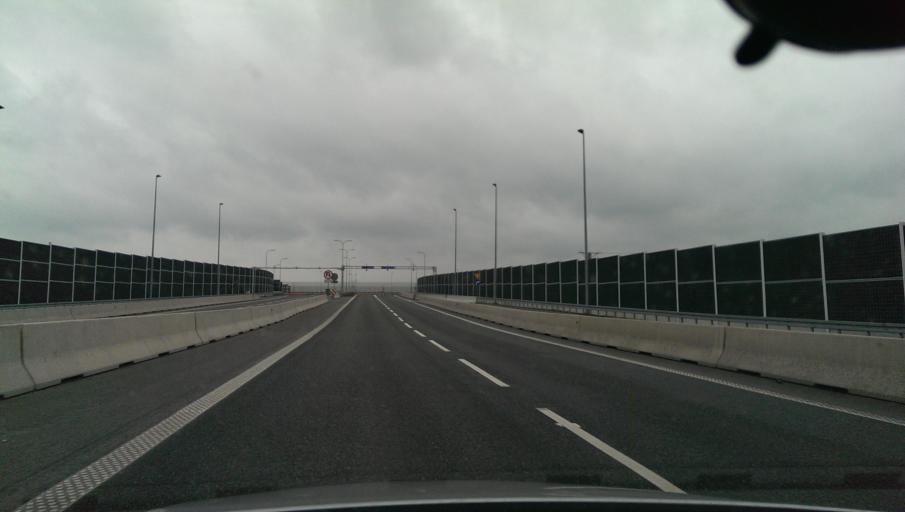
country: PL
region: Lesser Poland Voivodeship
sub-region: Powiat tarnowski
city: Wierzchoslawice
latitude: 50.0132
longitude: 20.8725
